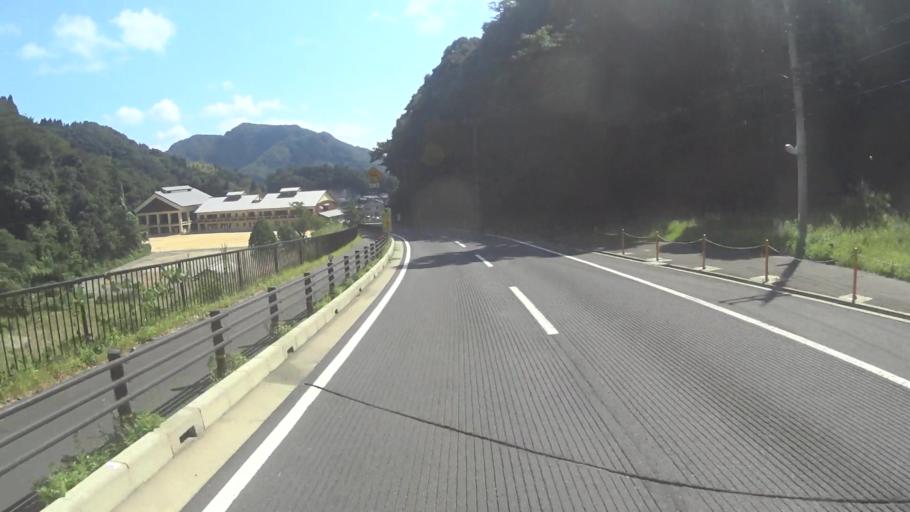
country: JP
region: Kyoto
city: Miyazu
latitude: 35.6798
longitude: 135.2858
